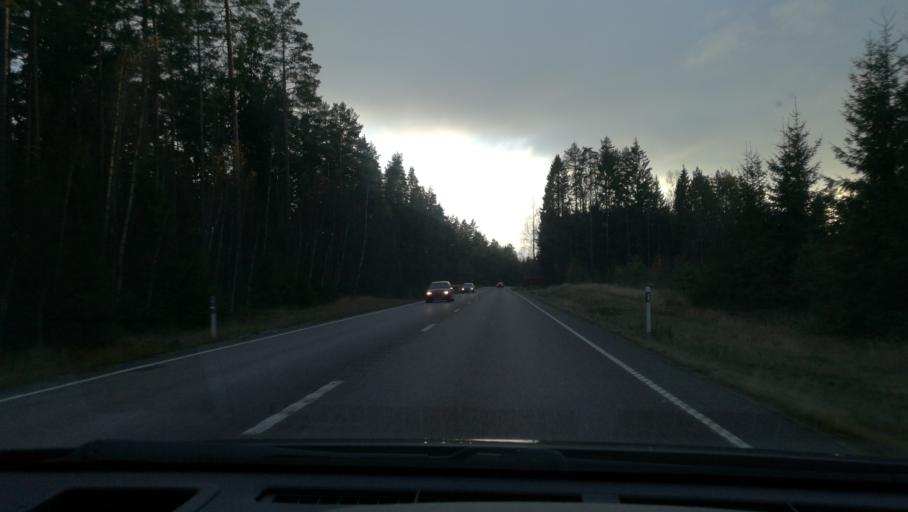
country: SE
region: Vaestmanland
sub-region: Kungsors Kommun
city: Kungsoer
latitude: 59.2224
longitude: 16.1020
